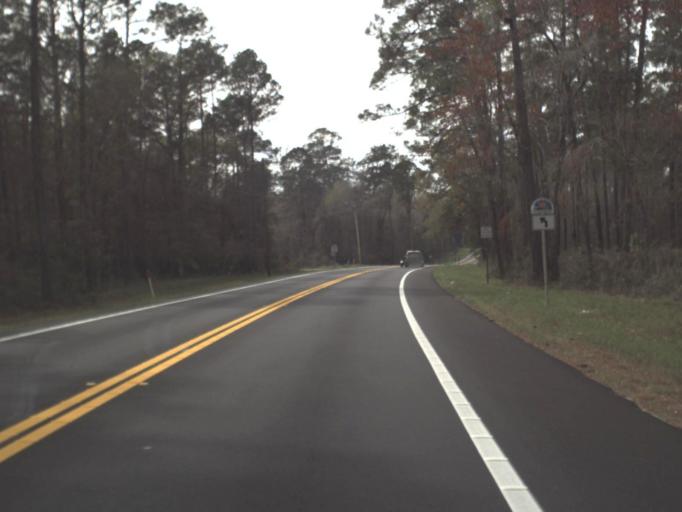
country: US
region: Florida
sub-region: Gadsden County
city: Quincy
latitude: 30.3884
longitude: -84.6327
